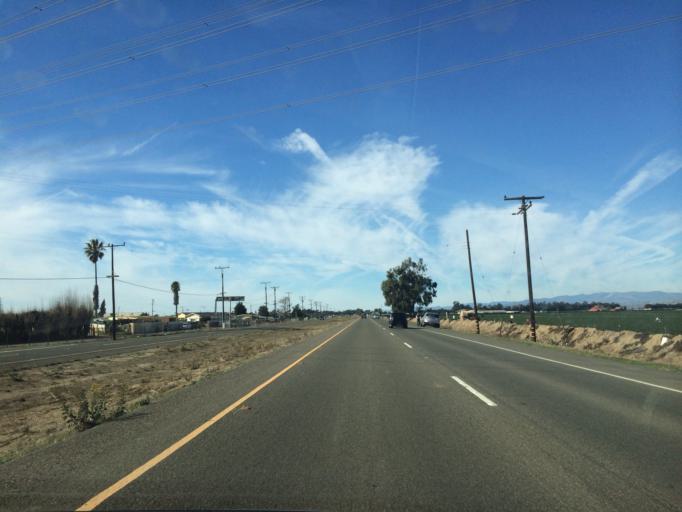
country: US
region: California
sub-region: Ventura County
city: Oxnard
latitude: 34.1541
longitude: -119.1229
